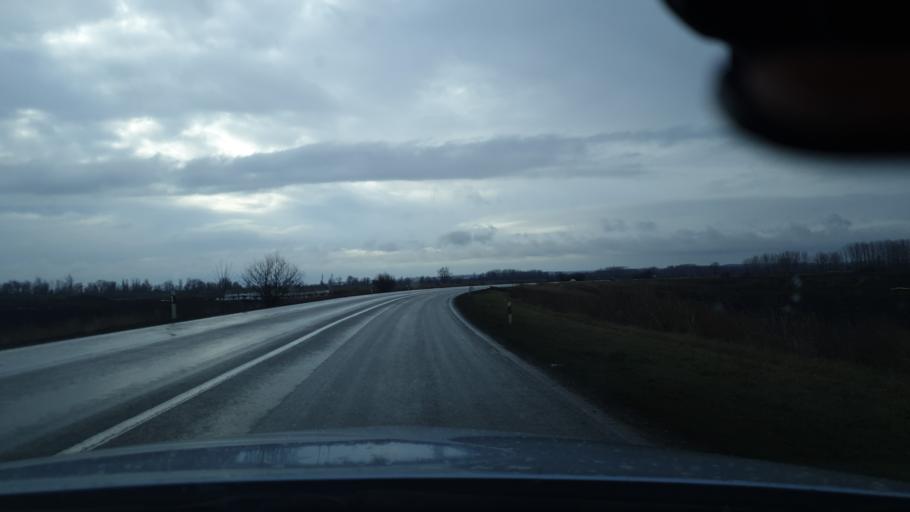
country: RS
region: Autonomna Pokrajina Vojvodina
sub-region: Juznobanatski Okrug
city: Kovin
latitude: 44.7175
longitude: 20.9637
